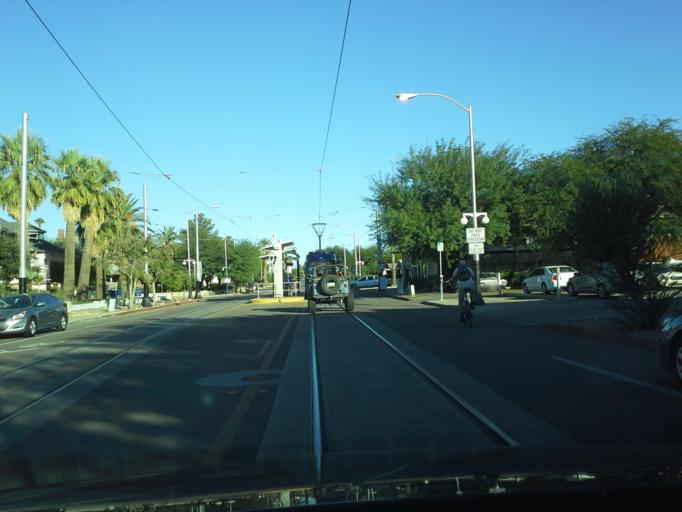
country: US
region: Arizona
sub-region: Pima County
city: South Tucson
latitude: 32.2317
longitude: -110.9650
